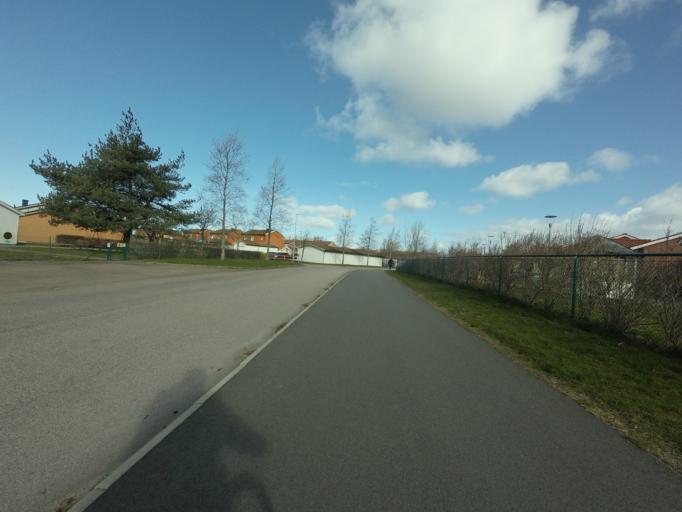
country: SE
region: Skane
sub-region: Hoganas Kommun
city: Hoganas
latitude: 56.1749
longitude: 12.5725
